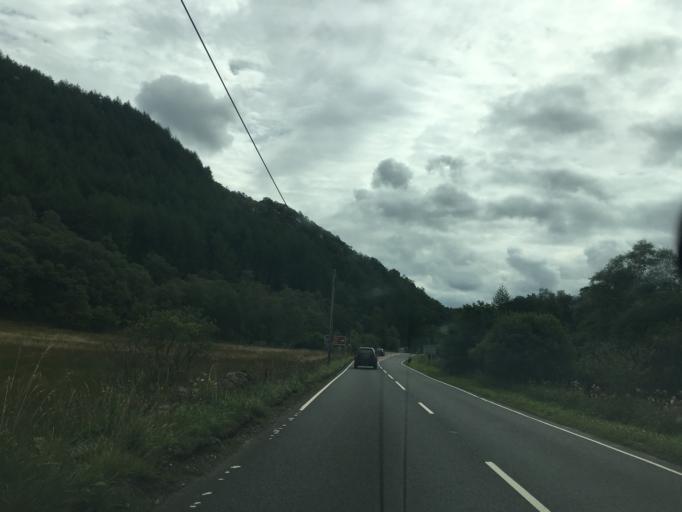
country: GB
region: Scotland
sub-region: Stirling
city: Callander
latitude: 56.2563
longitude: -4.2825
